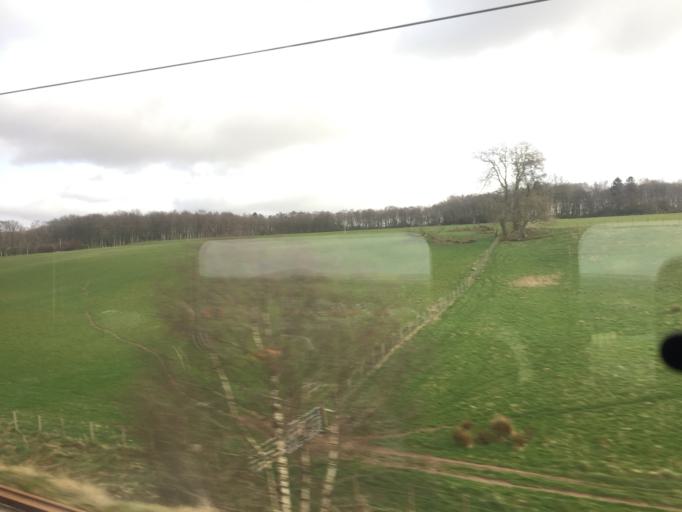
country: GB
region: Scotland
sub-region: Dumfries and Galloway
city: Lochmaben
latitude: 55.1934
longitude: -3.4037
